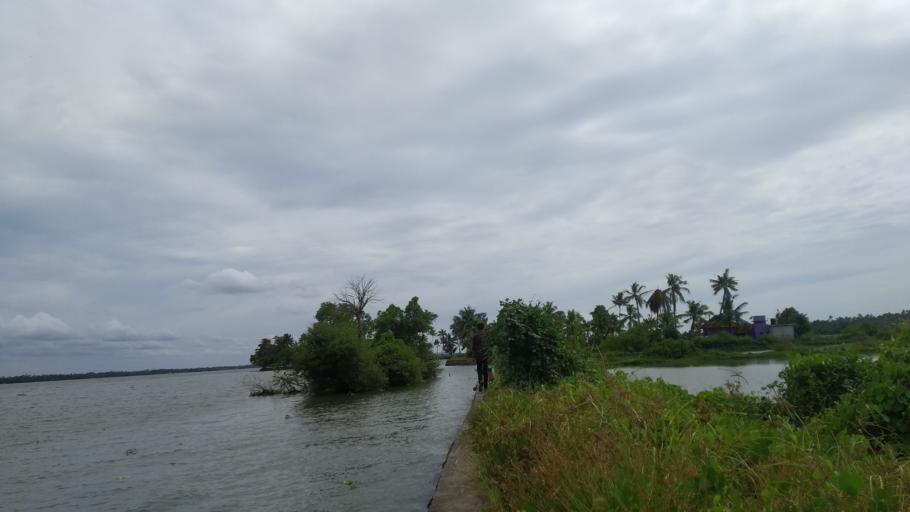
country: IN
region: Kerala
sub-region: Ernakulam
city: Elur
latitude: 10.0839
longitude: 76.2234
